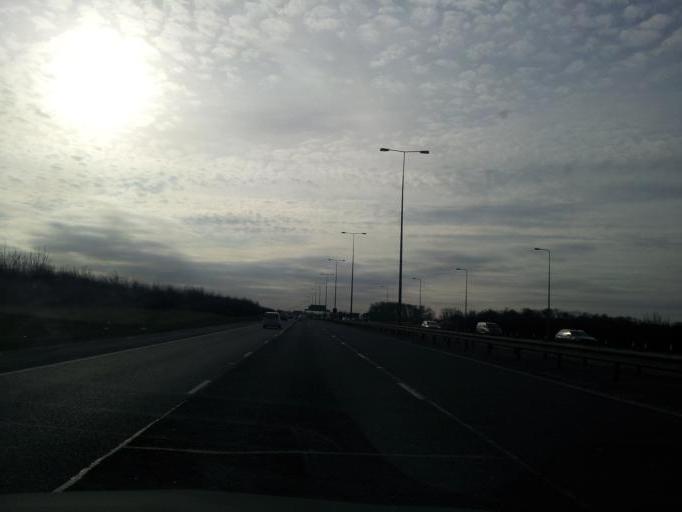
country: GB
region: England
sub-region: Cambridgeshire
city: Stilton
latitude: 52.5254
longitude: -0.3098
